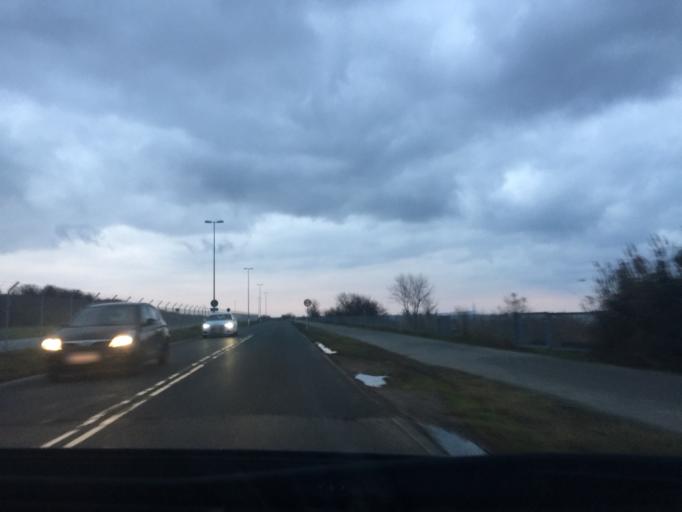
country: DK
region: Capital Region
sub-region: Dragor Kommune
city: Dragor
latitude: 55.6068
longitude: 12.6693
